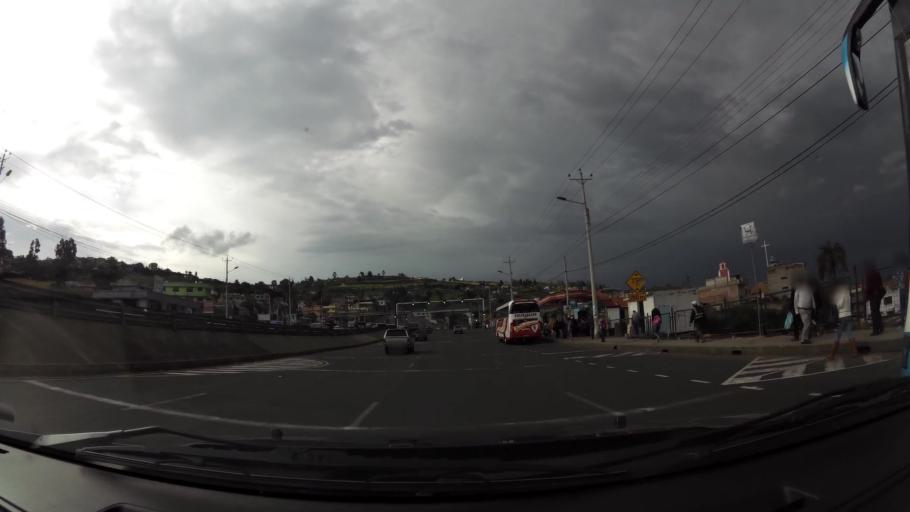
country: EC
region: Pichincha
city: Machachi
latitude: -0.4061
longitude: -78.5466
